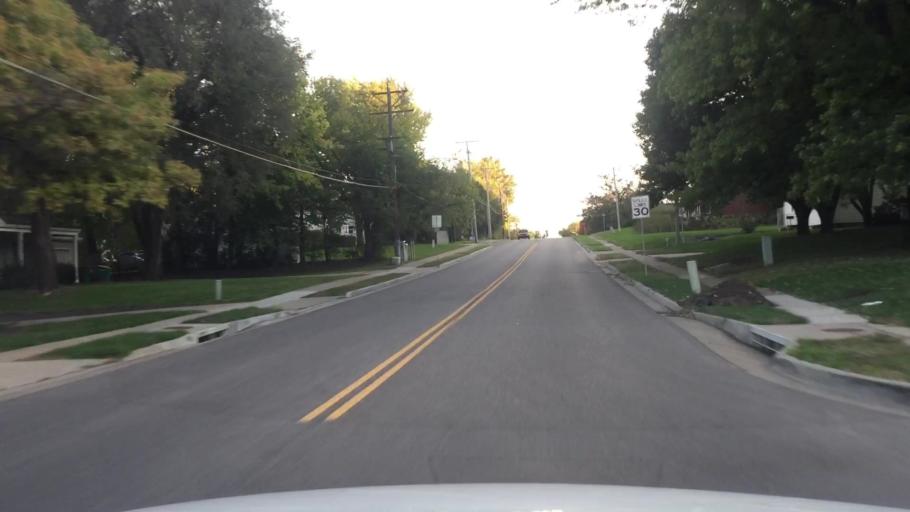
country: US
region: Kansas
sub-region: Johnson County
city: Shawnee
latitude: 39.0256
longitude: -94.7240
